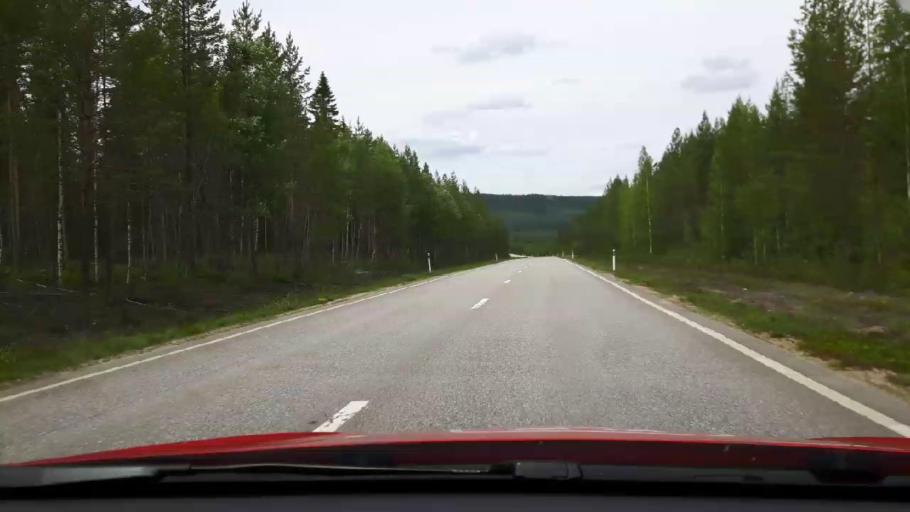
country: SE
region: Jaemtland
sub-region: Harjedalens Kommun
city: Sveg
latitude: 62.0855
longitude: 14.2518
